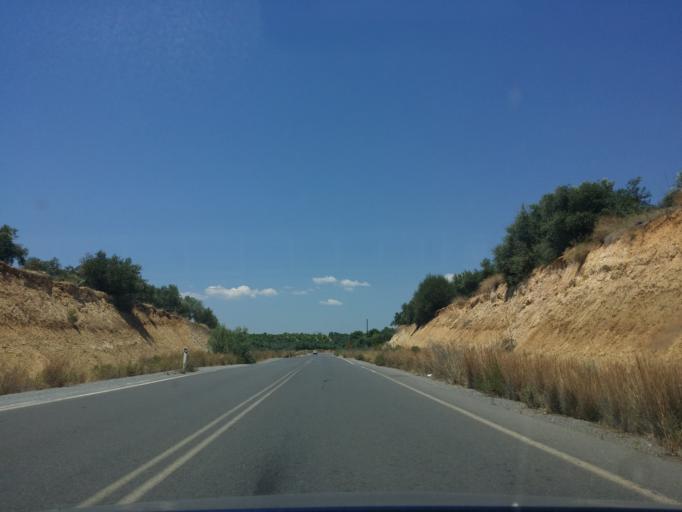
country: GR
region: Peloponnese
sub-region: Nomos Lakonias
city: Kato Glikovrisi
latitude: 36.8510
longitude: 22.7423
